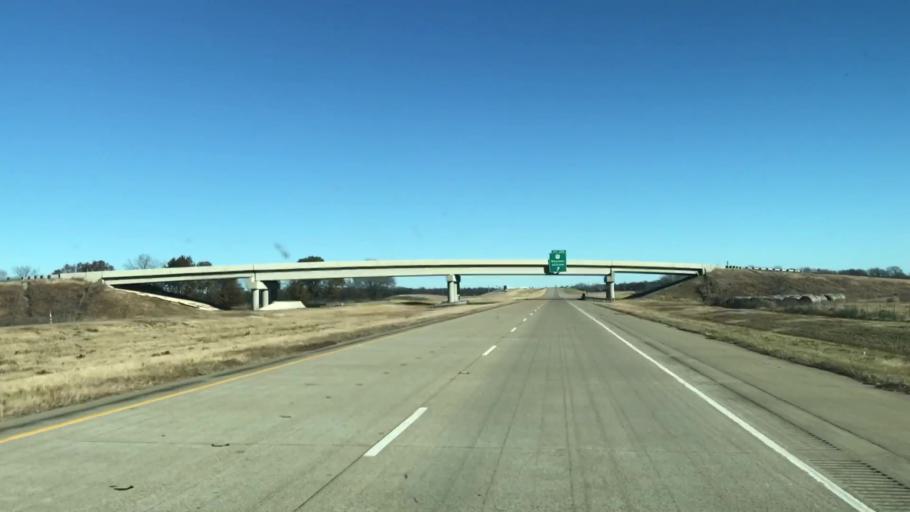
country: US
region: Louisiana
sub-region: Caddo Parish
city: Vivian
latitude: 32.8442
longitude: -93.8683
